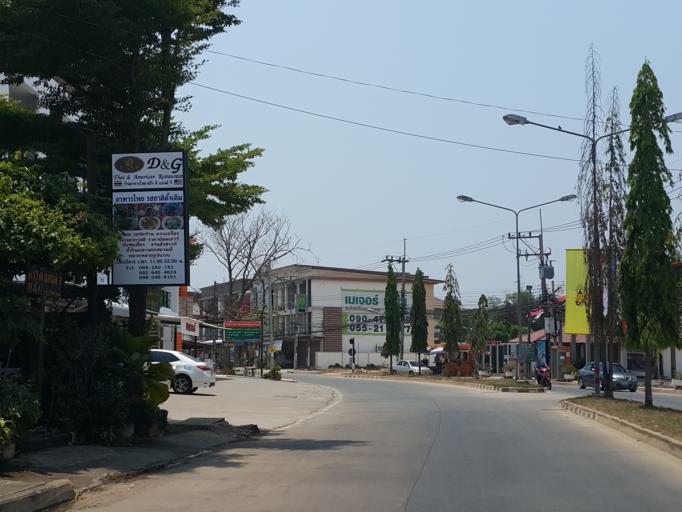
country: TH
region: Phitsanulok
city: Phitsanulok
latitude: 16.8154
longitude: 100.2447
